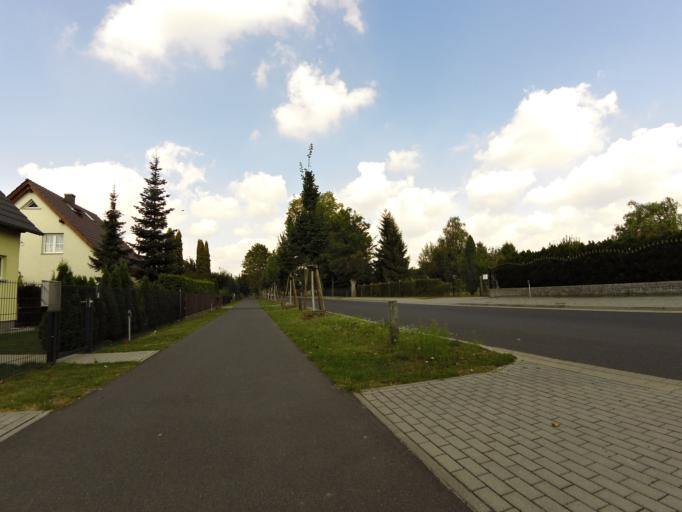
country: DE
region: Berlin
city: Lichtenrade
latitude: 52.3608
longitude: 13.4040
